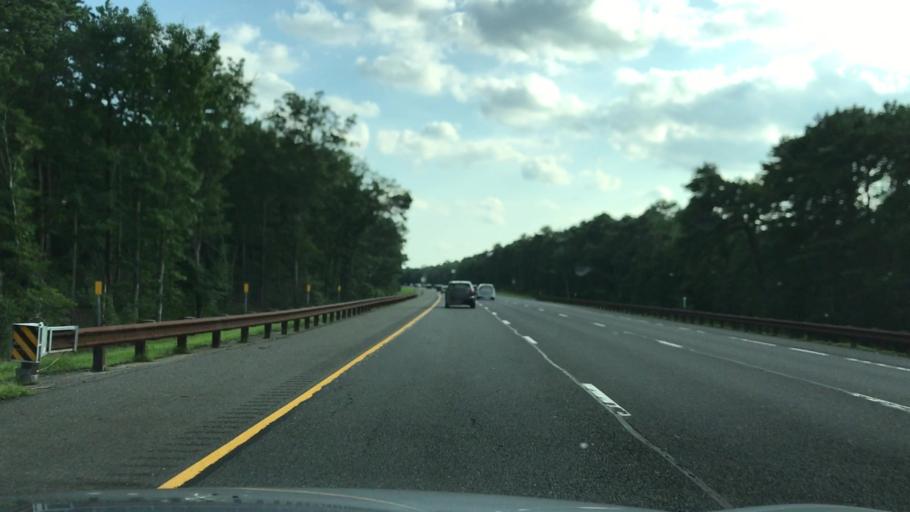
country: US
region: New Jersey
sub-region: Ocean County
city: Manahawkin
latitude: 39.6976
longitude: -74.2939
